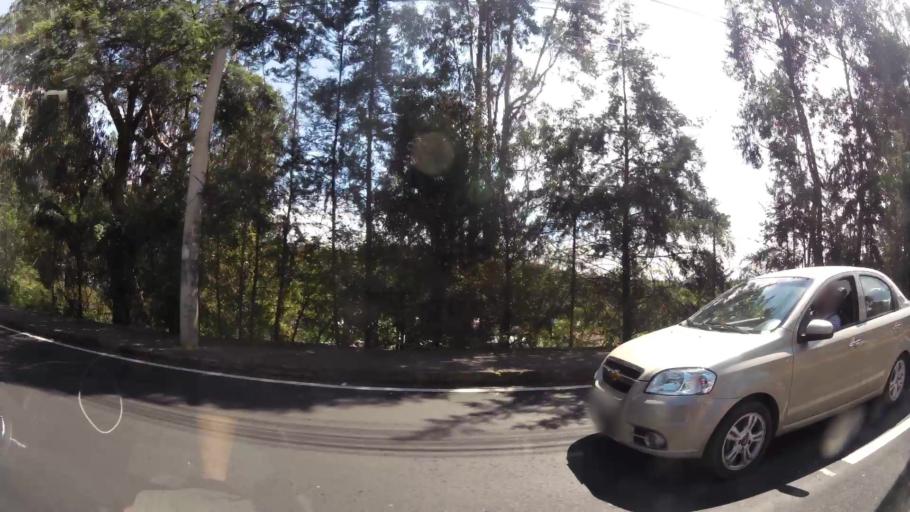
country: EC
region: Pichincha
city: Quito
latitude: -0.2103
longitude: -78.4190
